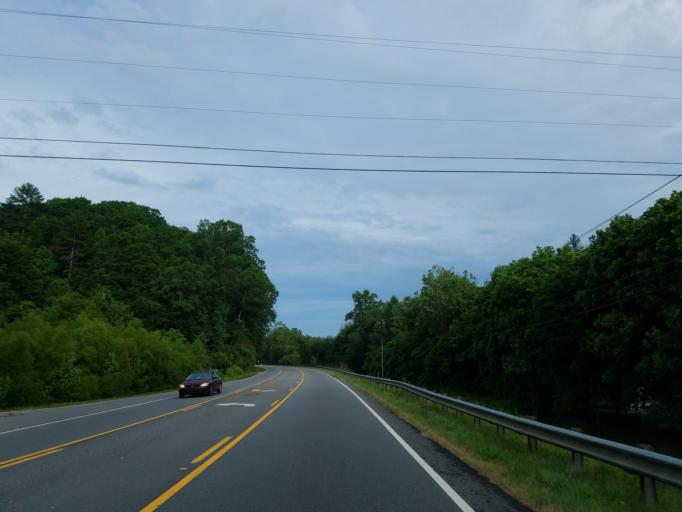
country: US
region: Georgia
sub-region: Lumpkin County
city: Dahlonega
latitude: 34.4709
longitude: -83.9755
